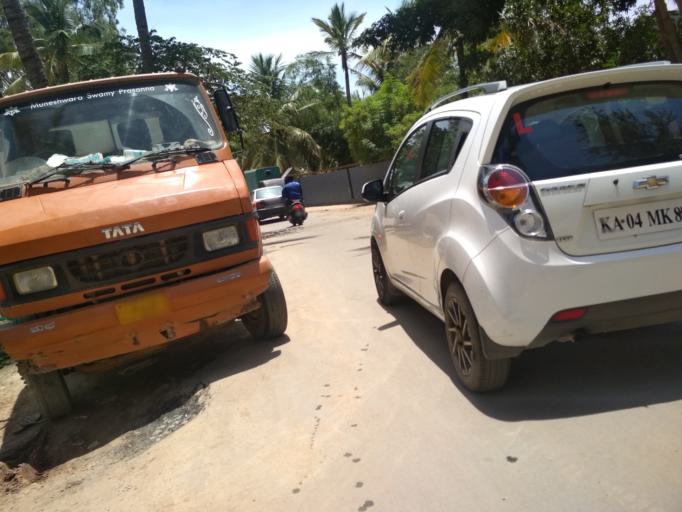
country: IN
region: Karnataka
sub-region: Bangalore Urban
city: Bangalore
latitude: 12.9300
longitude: 77.6715
